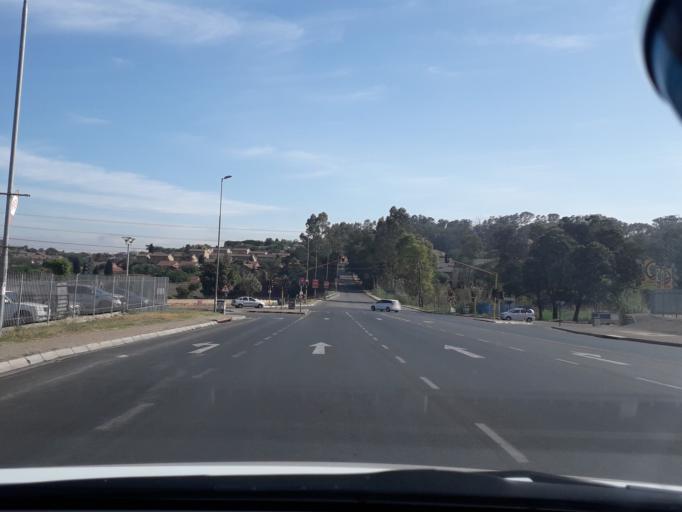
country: ZA
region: Gauteng
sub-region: City of Johannesburg Metropolitan Municipality
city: Roodepoort
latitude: -26.1134
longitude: 27.8960
